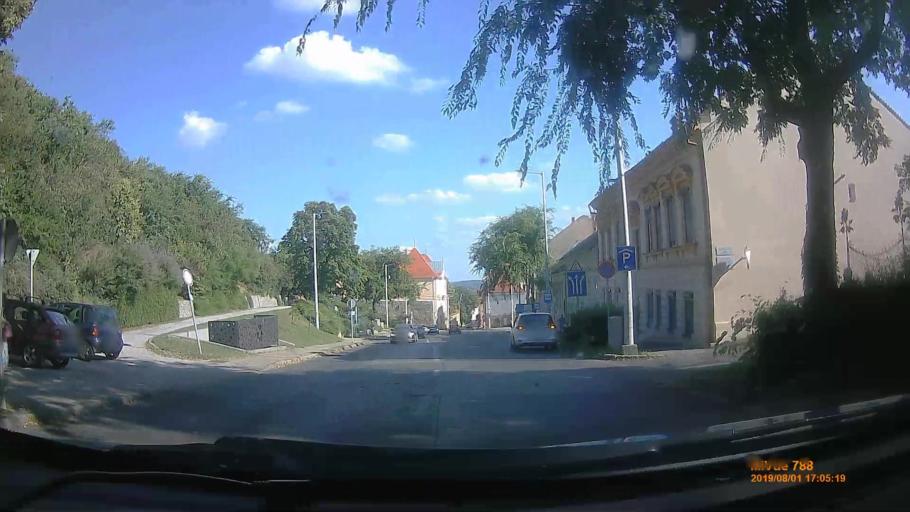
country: HU
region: Baranya
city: Pecs
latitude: 46.0808
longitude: 18.2263
